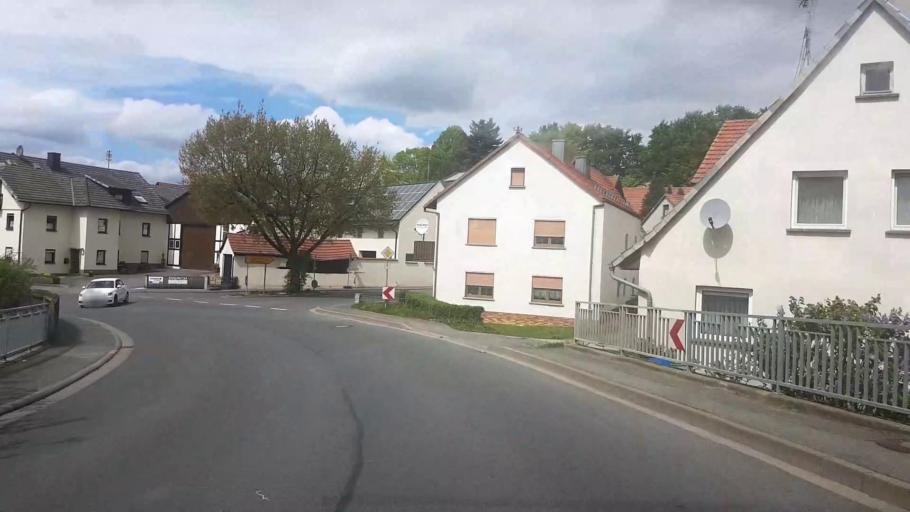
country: DE
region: Bavaria
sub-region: Upper Franconia
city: Untersiemau
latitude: 50.1858
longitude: 11.0153
